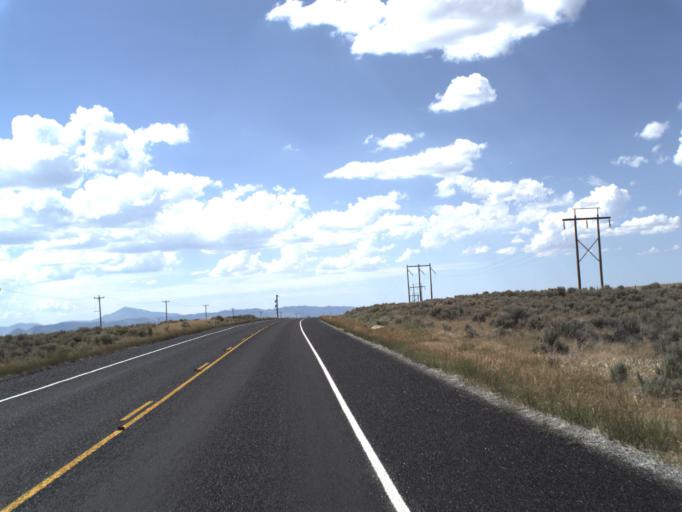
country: US
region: Idaho
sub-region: Minidoka County
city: Rupert
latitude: 41.9885
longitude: -113.1805
